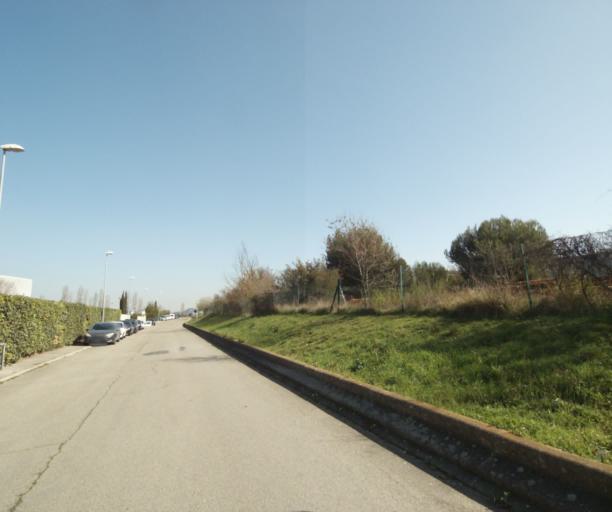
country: FR
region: Provence-Alpes-Cote d'Azur
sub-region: Departement des Bouches-du-Rhone
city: Cabries
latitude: 43.4246
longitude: 5.3898
